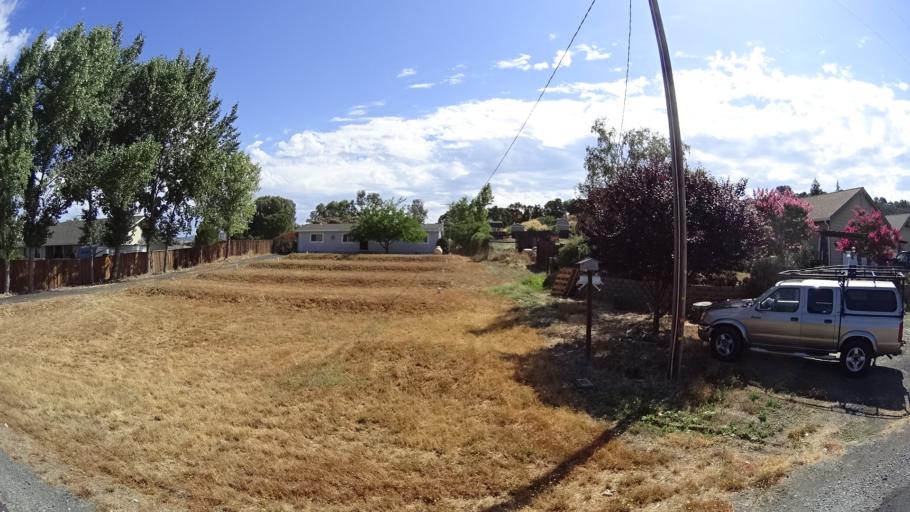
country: US
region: California
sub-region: Calaveras County
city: Copperopolis
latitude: 37.9325
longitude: -120.6402
